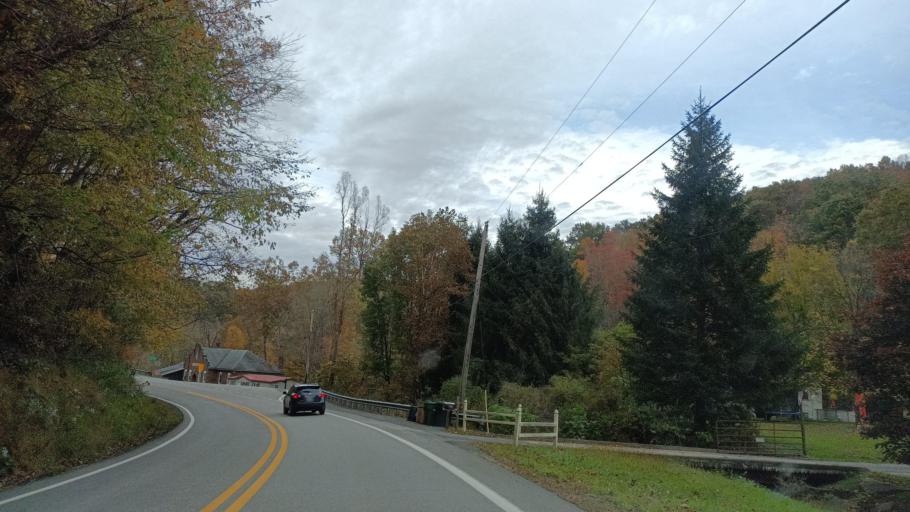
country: US
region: West Virginia
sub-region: Taylor County
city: Grafton
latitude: 39.3444
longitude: -79.9385
